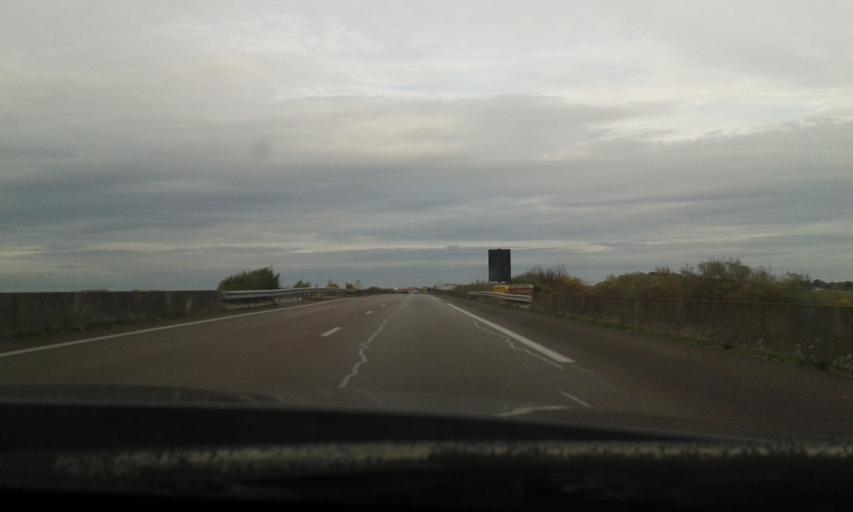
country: FR
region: Haute-Normandie
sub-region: Departement de l'Eure
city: La Madeleine-de-Nonancourt
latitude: 48.8603
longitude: 1.1782
